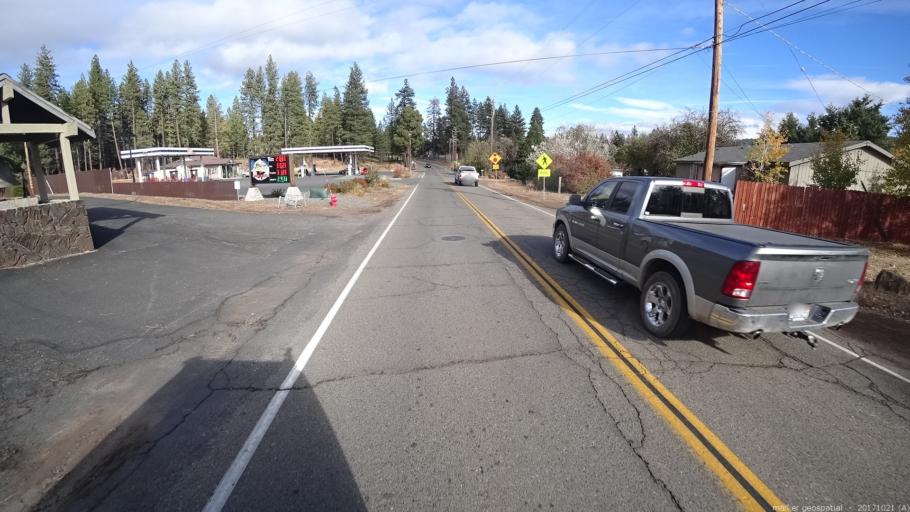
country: US
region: California
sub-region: Shasta County
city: Burney
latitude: 40.8761
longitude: -121.6761
